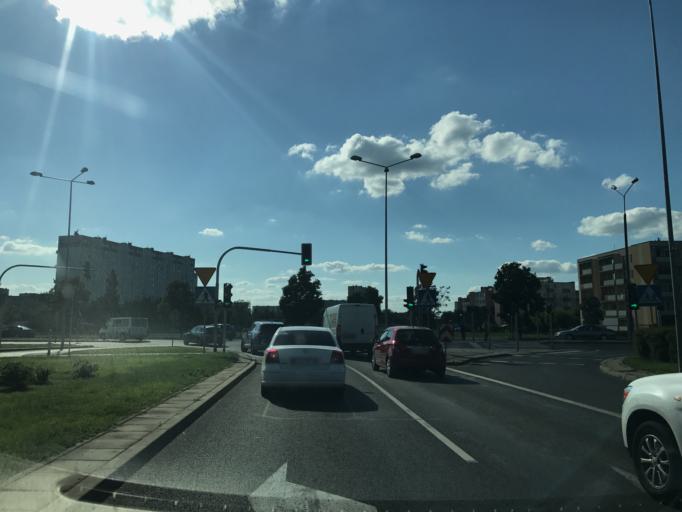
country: PL
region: Kujawsko-Pomorskie
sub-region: Wloclawek
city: Wloclawek
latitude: 52.6402
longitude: 19.0584
